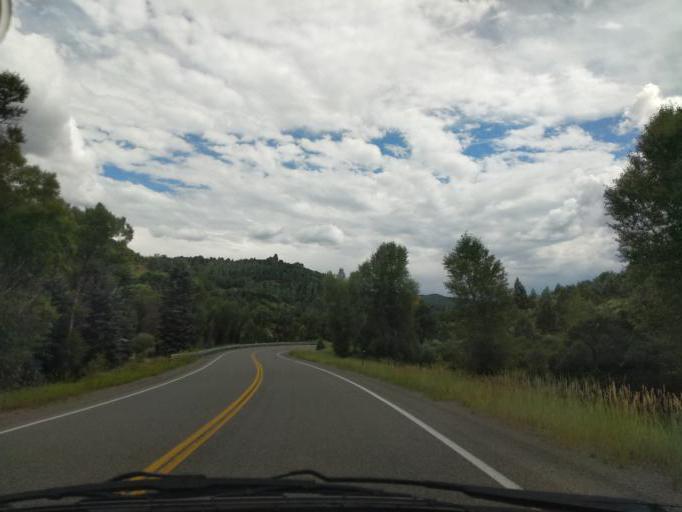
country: US
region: Colorado
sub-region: Delta County
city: Paonia
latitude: 39.0677
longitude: -107.3649
